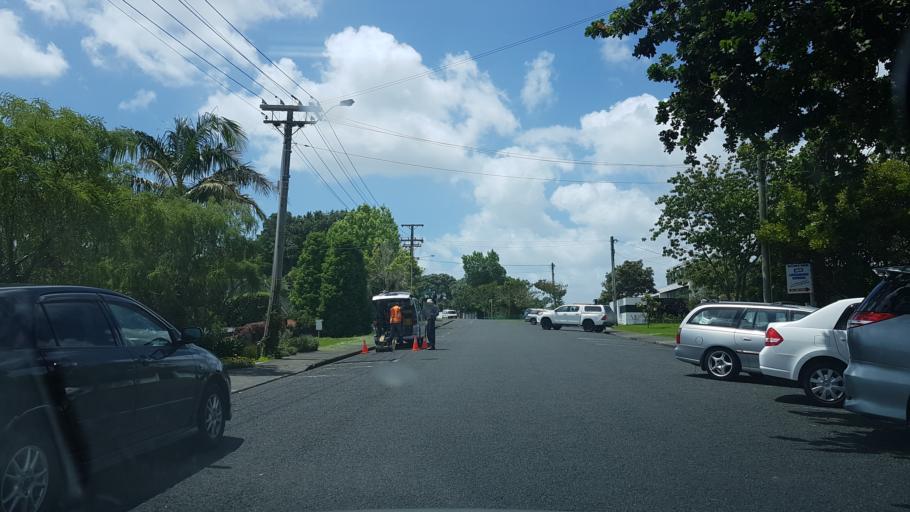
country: NZ
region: Auckland
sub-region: Auckland
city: North Shore
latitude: -36.7903
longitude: 174.6808
